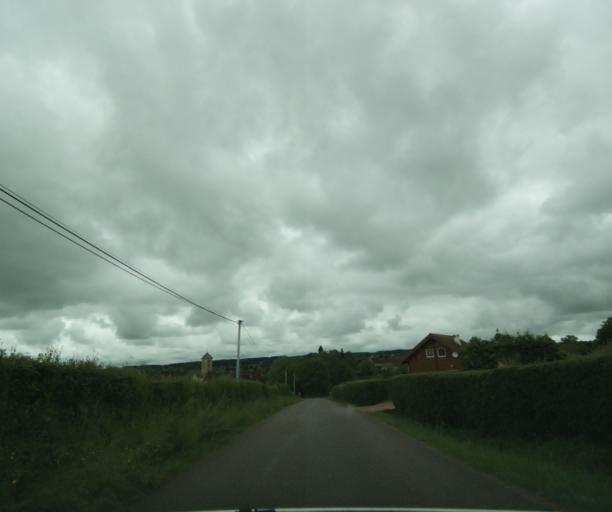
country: FR
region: Bourgogne
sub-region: Departement de Saone-et-Loire
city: Charolles
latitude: 46.4708
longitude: 4.3380
